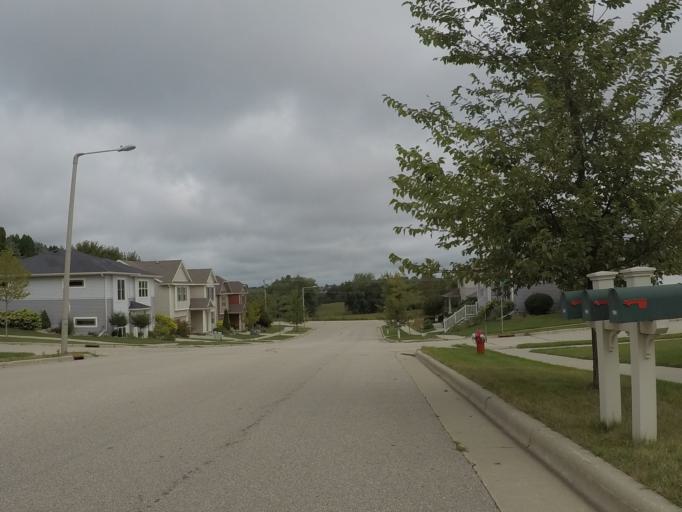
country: US
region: Wisconsin
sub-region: Dane County
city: Verona
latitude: 43.0447
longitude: -89.5469
